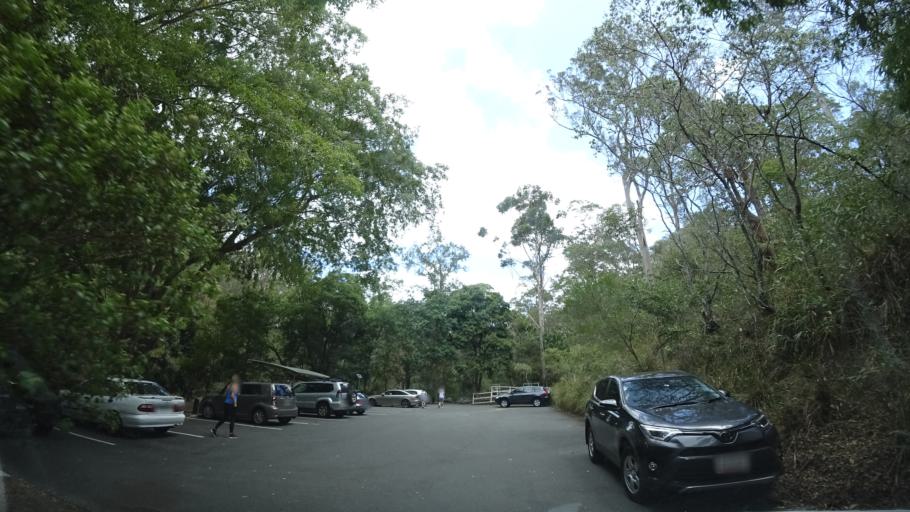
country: AU
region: Queensland
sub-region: Brisbane
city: Taringa
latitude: -27.4742
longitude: 152.9654
